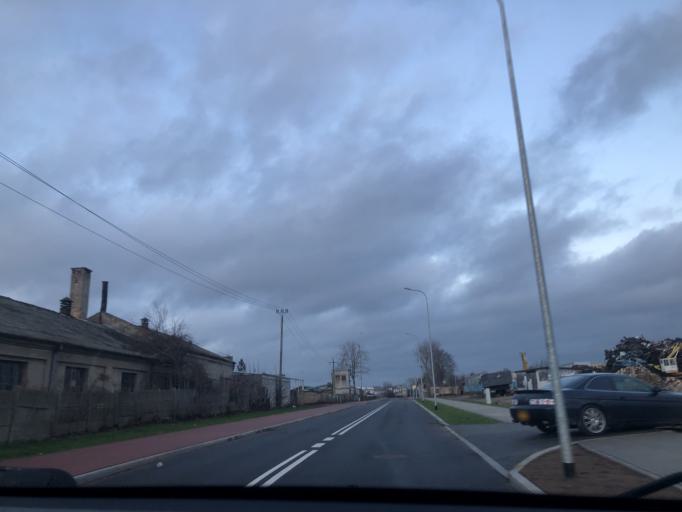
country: PL
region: Podlasie
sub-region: Lomza
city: Lomza
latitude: 53.1715
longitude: 22.0616
